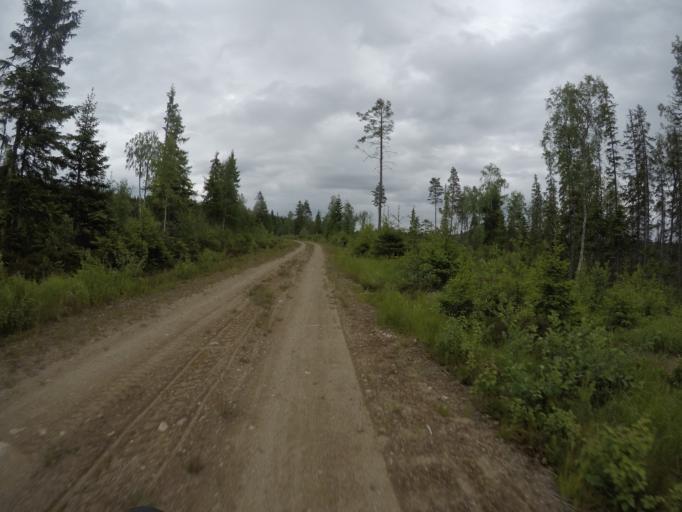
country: SE
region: Dalarna
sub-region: Ludvika Kommun
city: Abborrberget
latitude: 60.0585
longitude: 14.5658
